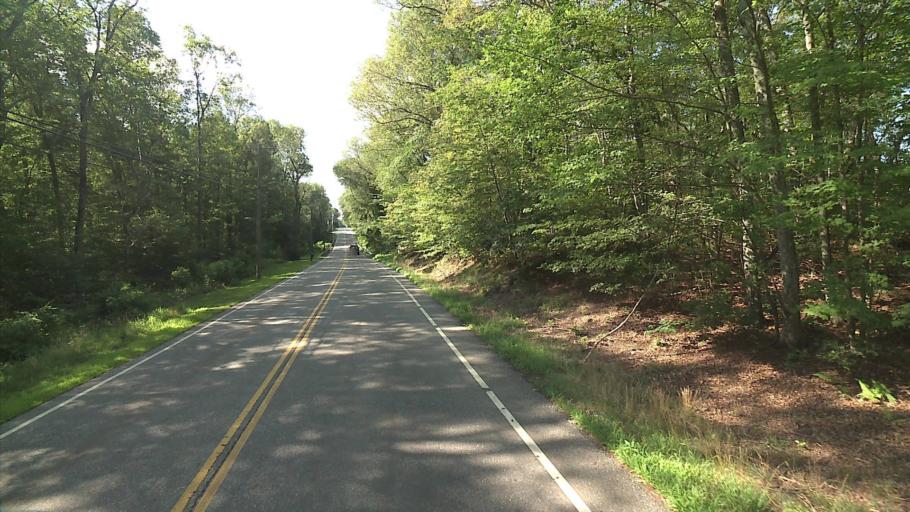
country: US
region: Connecticut
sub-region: New London County
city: Montville Center
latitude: 41.5247
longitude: -72.2064
